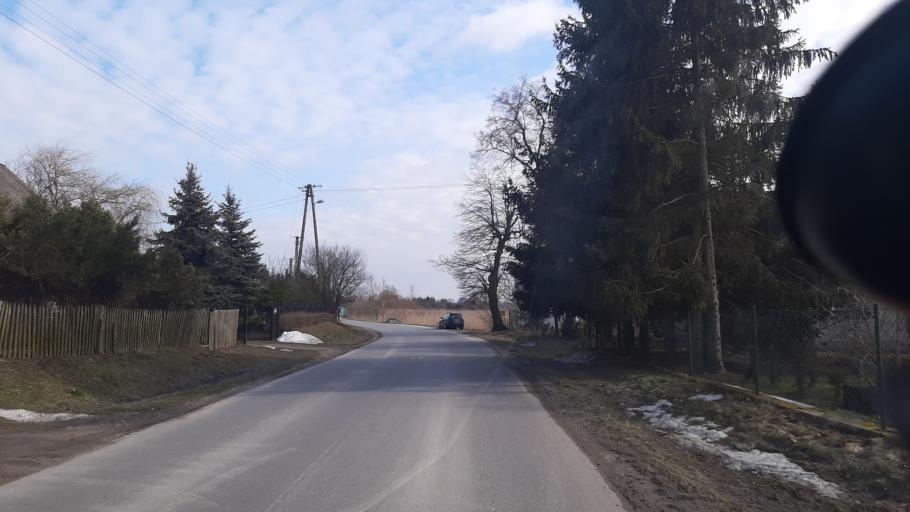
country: PL
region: Lublin Voivodeship
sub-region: Powiat lubartowski
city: Uscimow Stary
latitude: 51.4788
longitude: 22.9209
